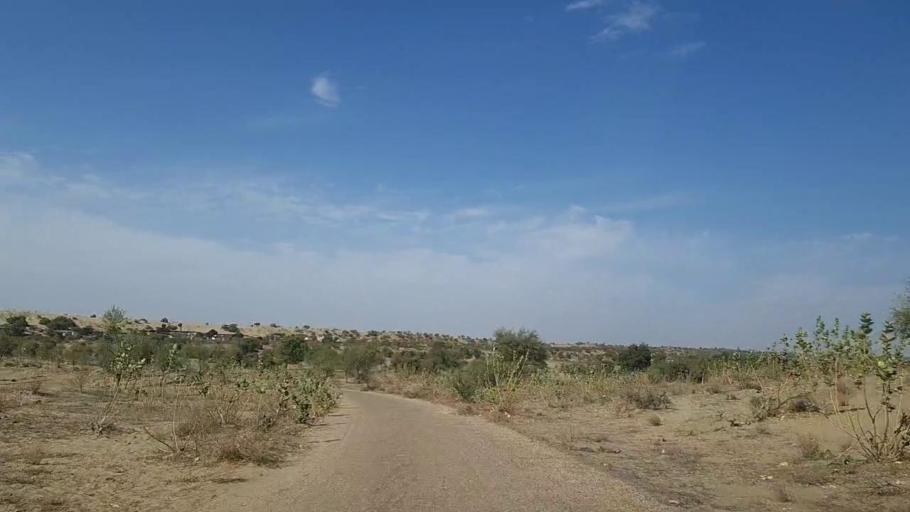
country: PK
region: Sindh
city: Naukot
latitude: 24.8311
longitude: 69.5480
